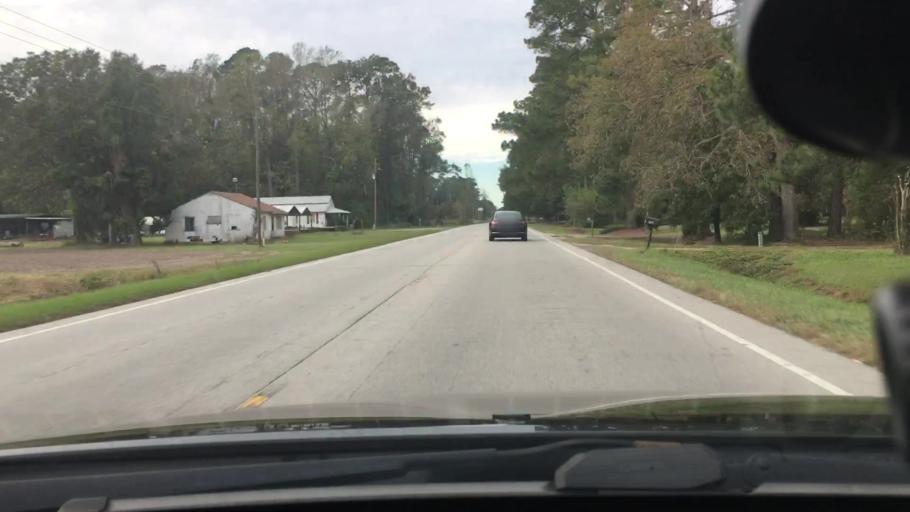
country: US
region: North Carolina
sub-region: Craven County
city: Vanceboro
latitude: 35.2646
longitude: -77.1052
